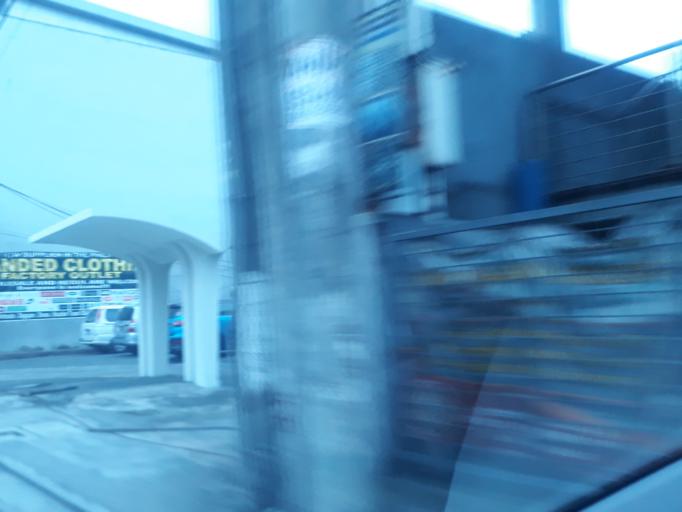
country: PH
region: Calabarzon
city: Del Monte
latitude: 14.6221
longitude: 121.0066
